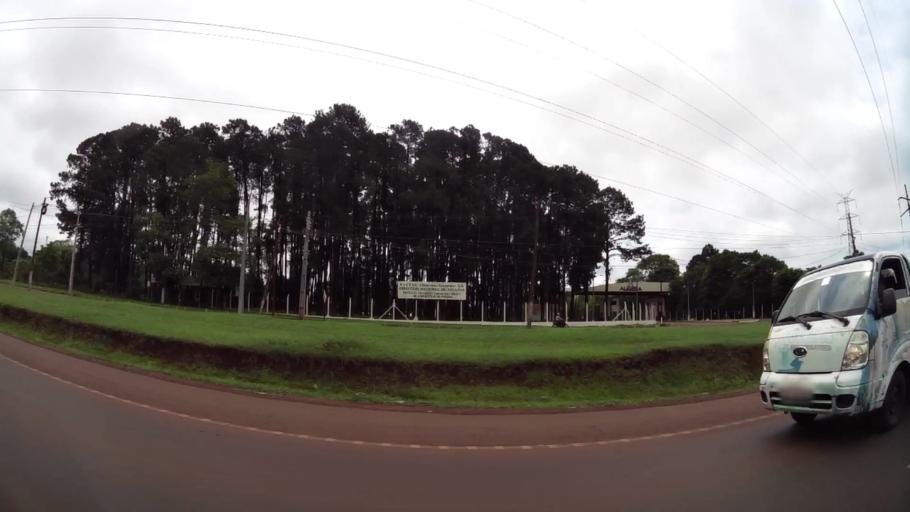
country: PY
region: Alto Parana
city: Ciudad del Este
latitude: -25.4931
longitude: -54.7229
